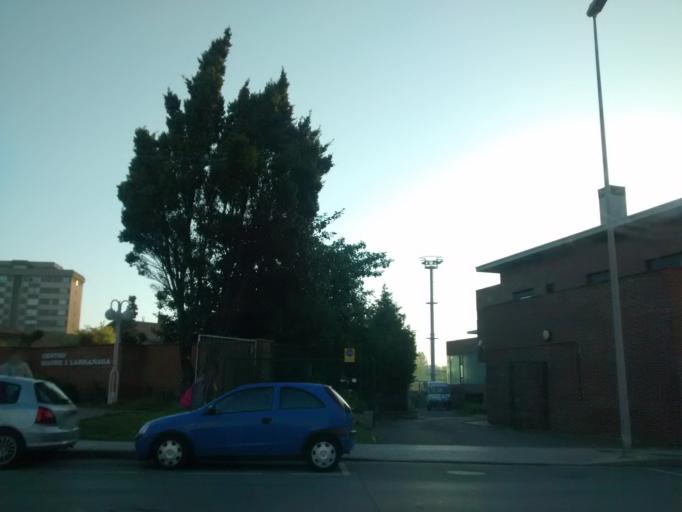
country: ES
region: Asturias
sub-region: Province of Asturias
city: Gijon
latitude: 43.5293
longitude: -5.6419
